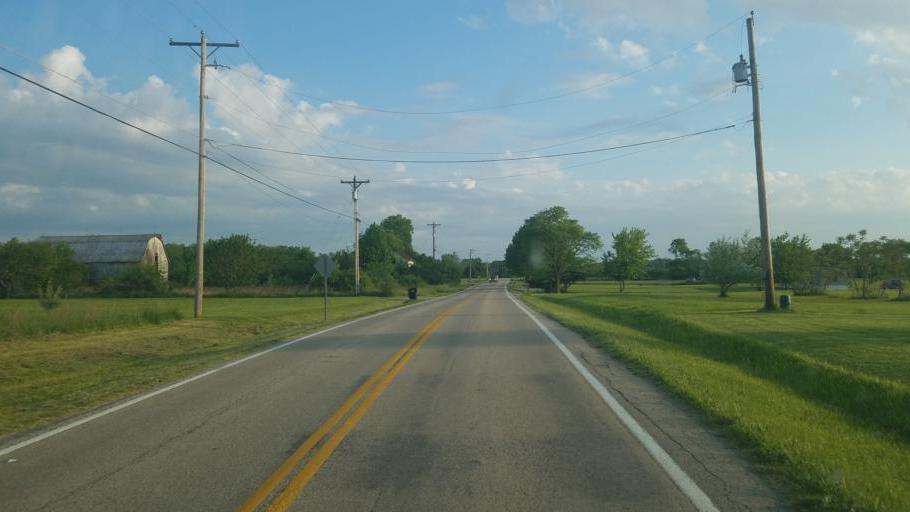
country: US
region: Ohio
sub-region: Highland County
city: Leesburg
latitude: 39.3590
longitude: -83.5888
